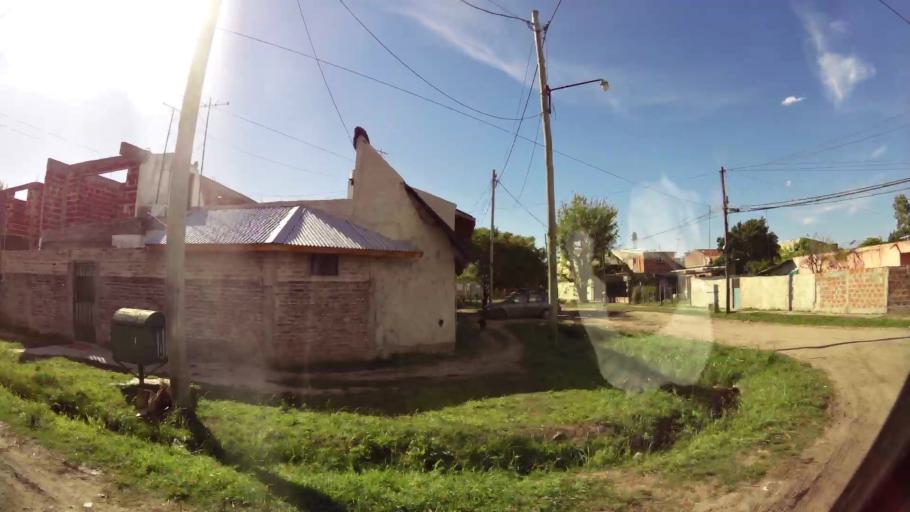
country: AR
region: Buenos Aires
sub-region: Partido de Almirante Brown
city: Adrogue
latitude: -34.8221
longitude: -58.3414
